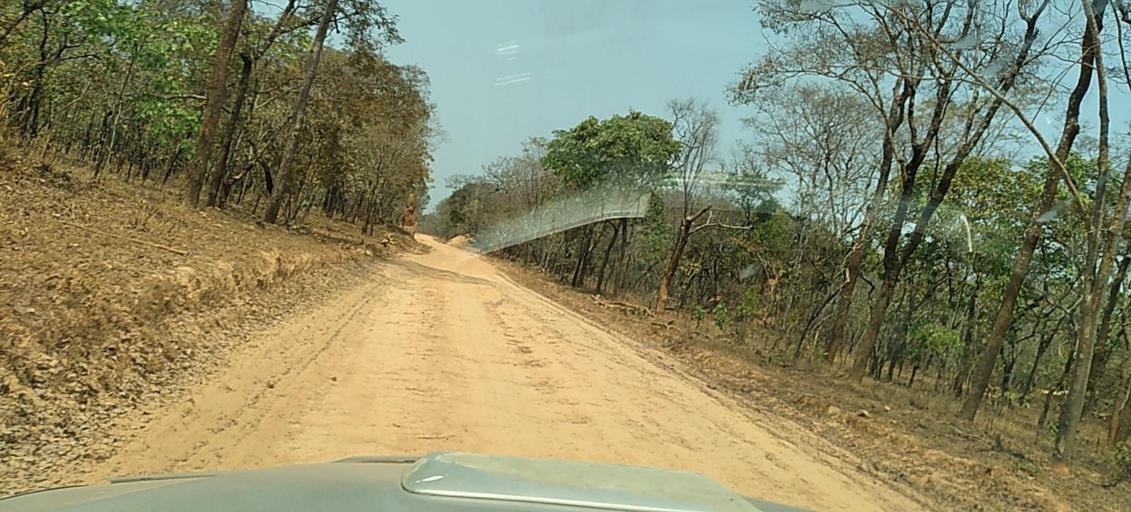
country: ZM
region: North-Western
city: Kasempa
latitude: -13.6628
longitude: 26.2756
